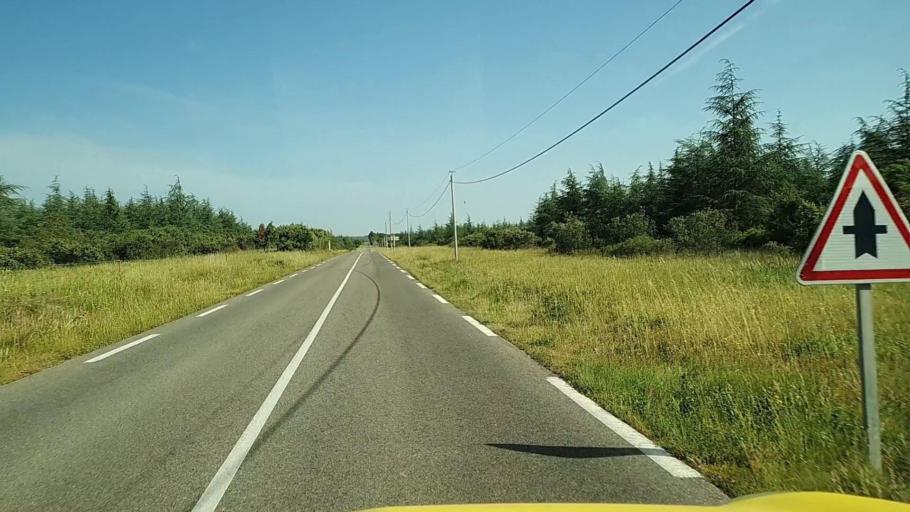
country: FR
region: Languedoc-Roussillon
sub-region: Departement du Gard
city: Montaren-et-Saint-Mediers
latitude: 44.0711
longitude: 4.3951
